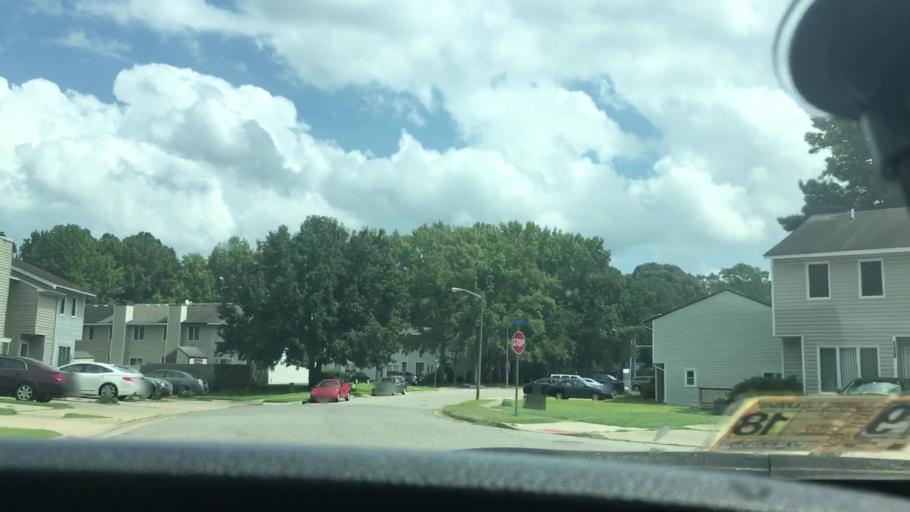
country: US
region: Virginia
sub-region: City of Portsmouth
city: Portsmouth Heights
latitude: 36.8583
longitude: -76.4097
